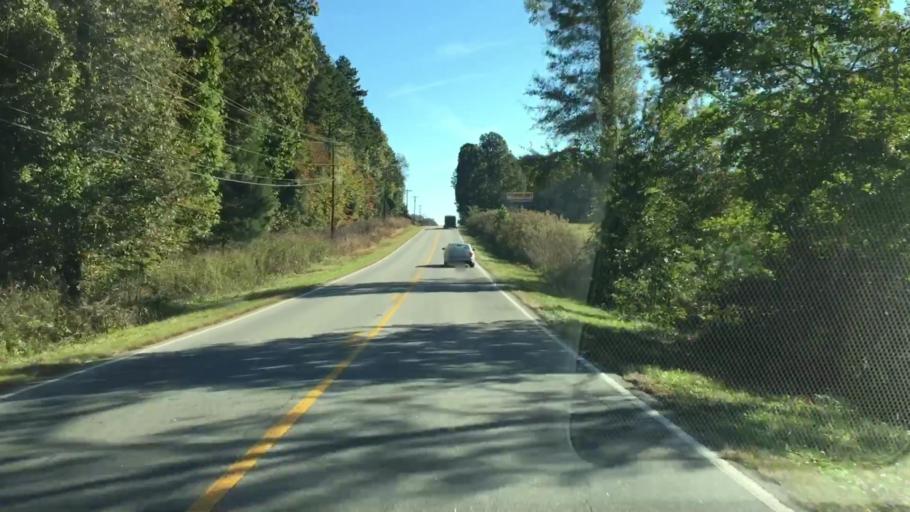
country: US
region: North Carolina
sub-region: Rowan County
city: China Grove
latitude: 35.6481
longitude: -80.6272
